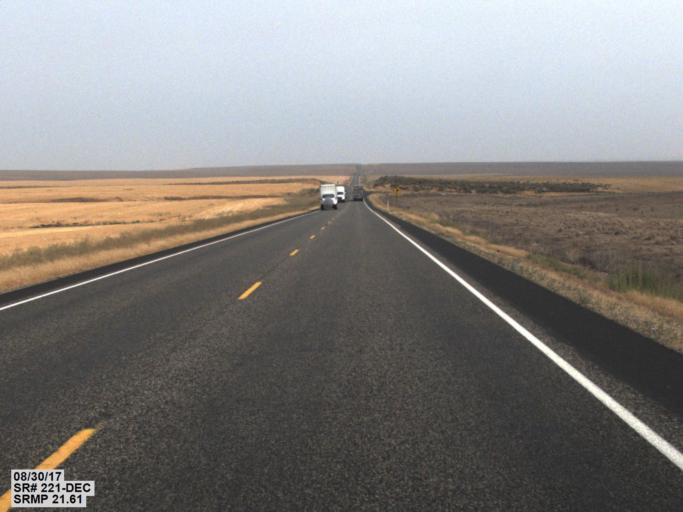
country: US
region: Washington
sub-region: Benton County
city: Prosser
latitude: 46.1873
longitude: -119.6914
